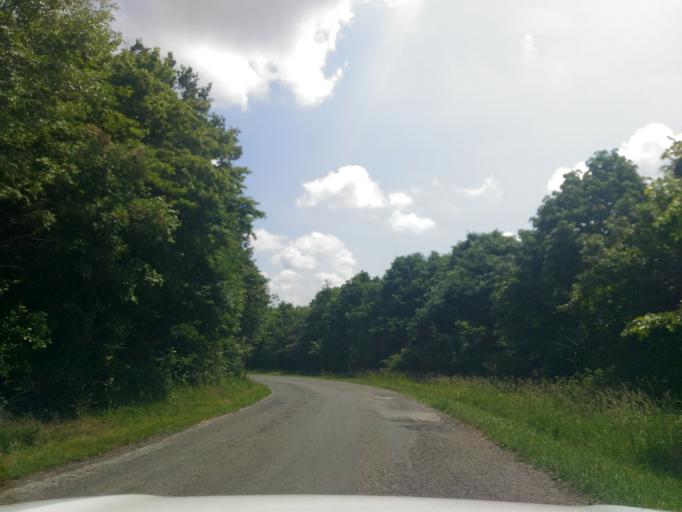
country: HU
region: Baranya
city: Pecs
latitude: 46.1184
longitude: 18.2056
